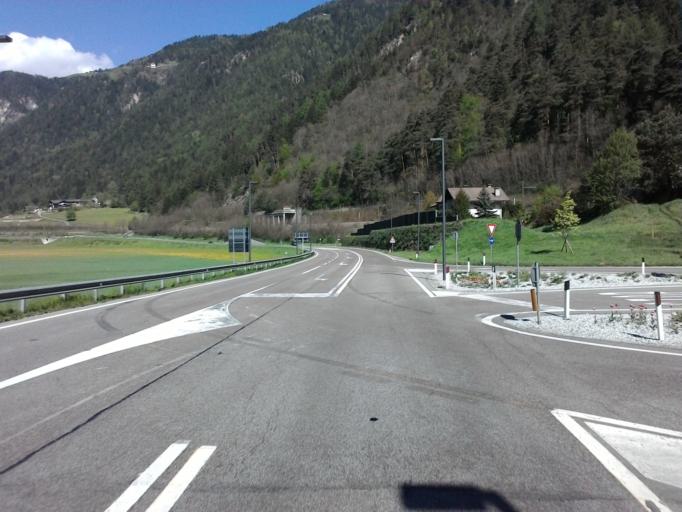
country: IT
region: Trentino-Alto Adige
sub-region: Bolzano
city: Vandoies - Vintl
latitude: 46.8162
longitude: 11.7143
